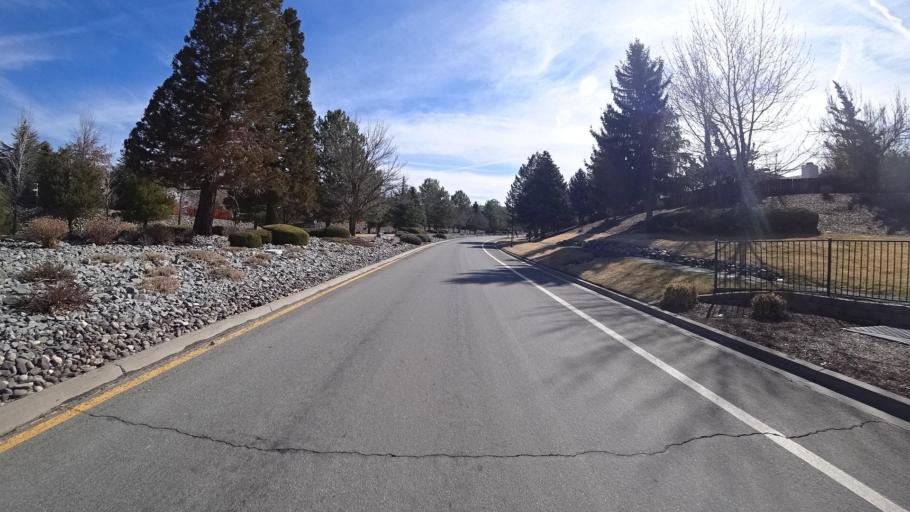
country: US
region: Nevada
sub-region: Washoe County
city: Spanish Springs
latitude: 39.5856
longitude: -119.7115
